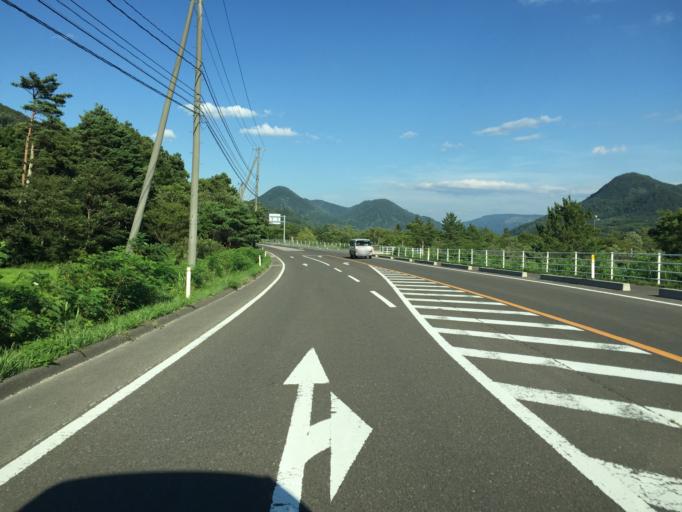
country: JP
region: Miyagi
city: Shiroishi
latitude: 37.9831
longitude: 140.4681
